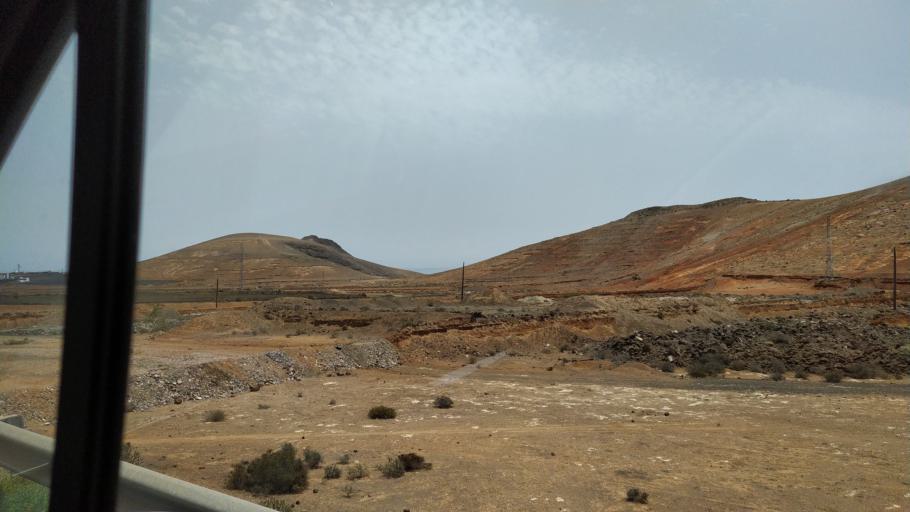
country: ES
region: Canary Islands
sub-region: Provincia de Las Palmas
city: Yaiza
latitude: 28.9255
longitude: -13.7638
